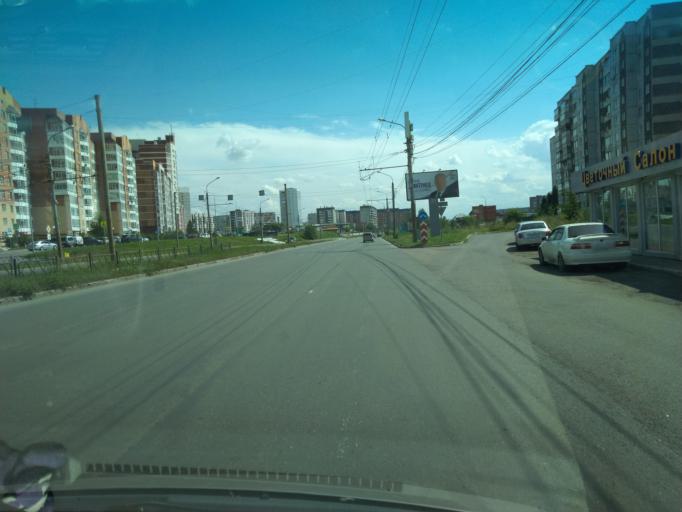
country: RU
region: Krasnoyarskiy
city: Solnechnyy
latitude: 56.0613
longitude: 92.9345
